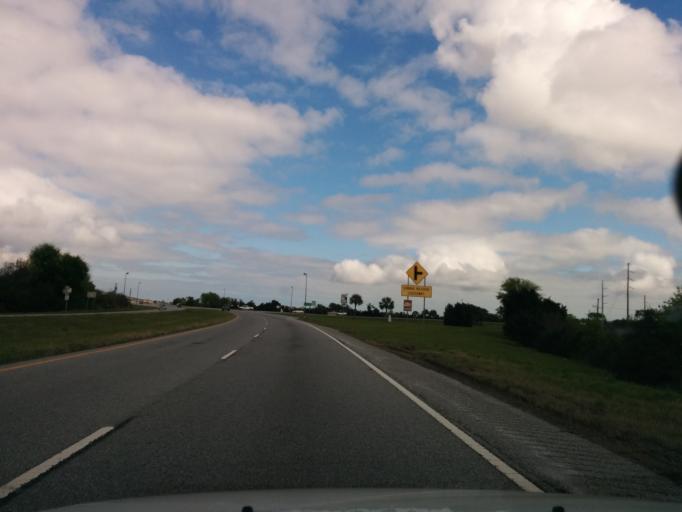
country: US
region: Georgia
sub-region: Glynn County
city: Brunswick
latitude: 31.1052
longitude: -81.4956
